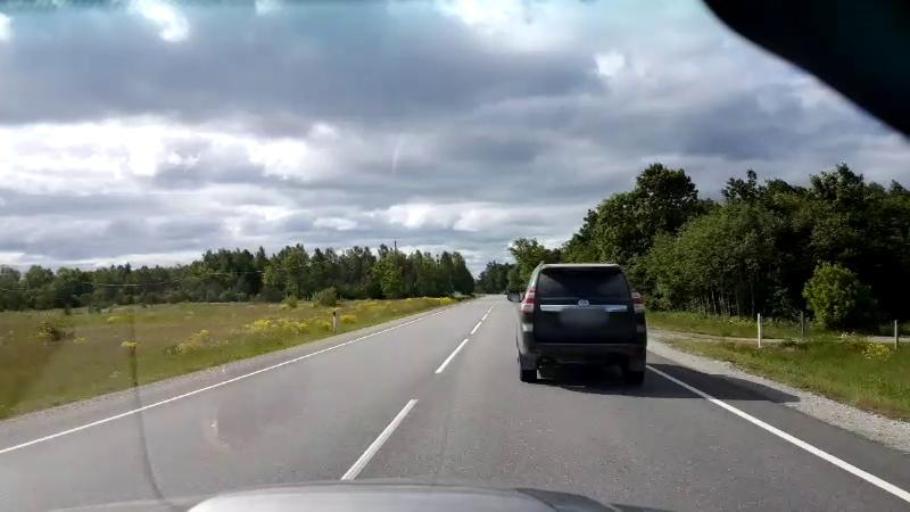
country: EE
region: Raplamaa
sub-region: Maerjamaa vald
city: Marjamaa
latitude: 58.9696
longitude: 24.4760
